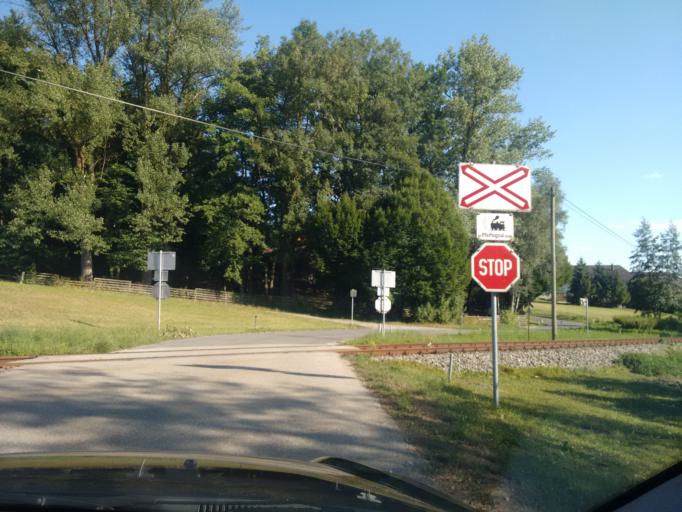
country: AT
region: Upper Austria
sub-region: Wels-Land
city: Buchkirchen
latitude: 48.2331
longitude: 13.9720
